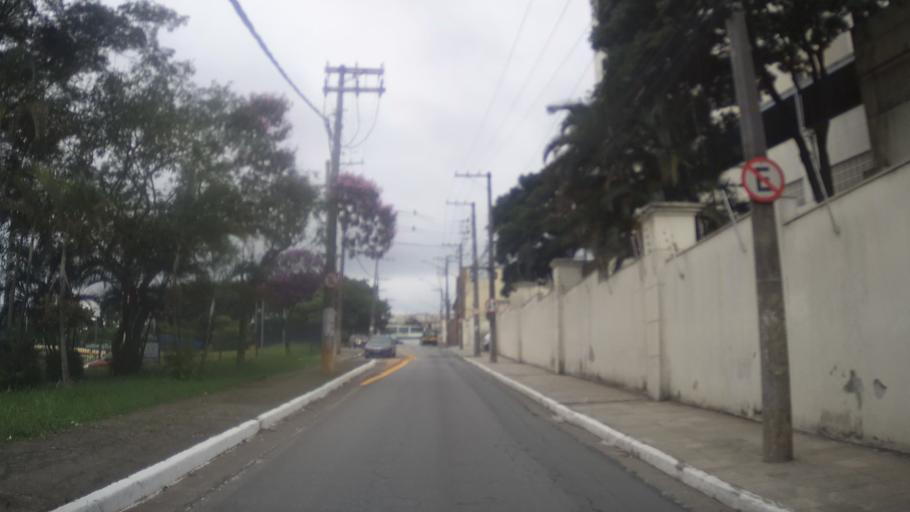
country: BR
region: Sao Paulo
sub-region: Guarulhos
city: Guarulhos
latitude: -23.4435
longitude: -46.5381
